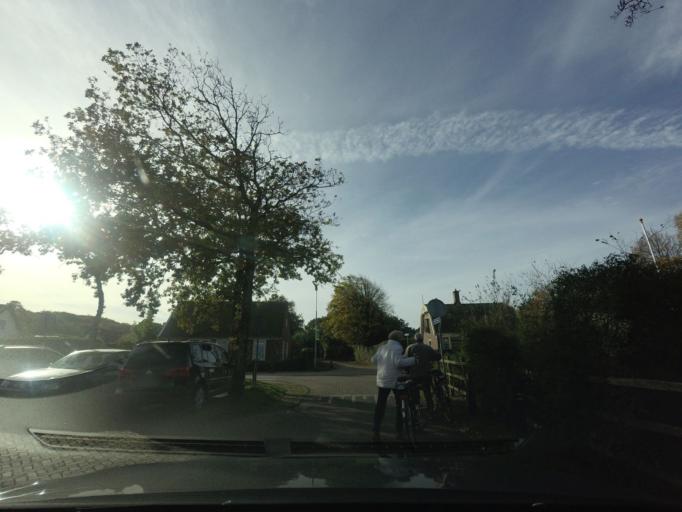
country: NL
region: North Holland
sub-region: Gemeente Bergen
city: Egmond aan Zee
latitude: 52.7225
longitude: 4.6626
